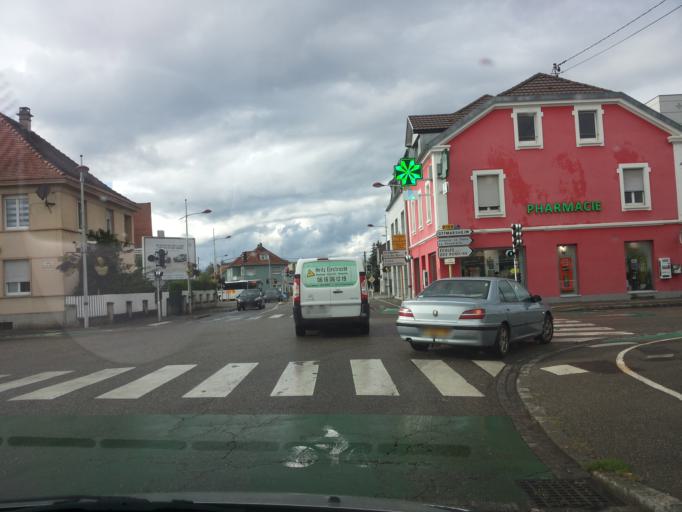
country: FR
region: Alsace
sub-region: Departement du Haut-Rhin
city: Rixheim
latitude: 47.7496
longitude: 7.4074
